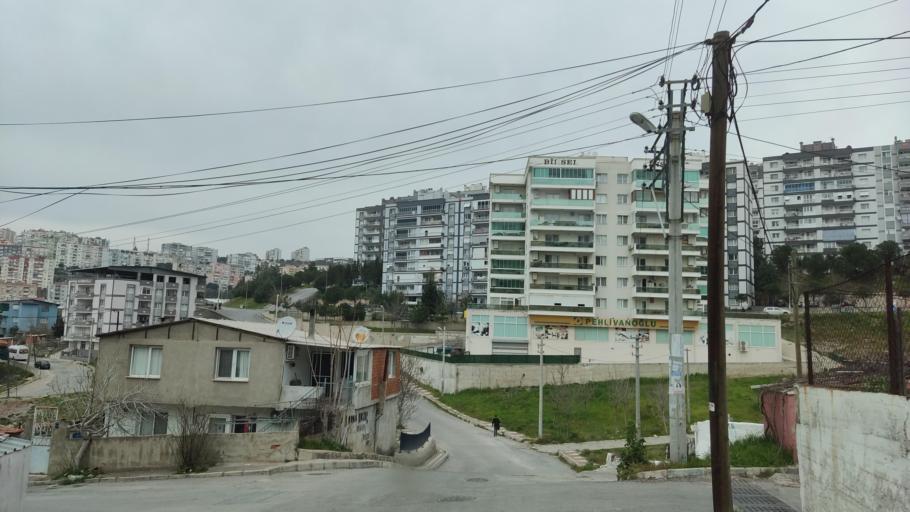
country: TR
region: Izmir
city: Karsiyaka
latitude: 38.5014
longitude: 27.0724
